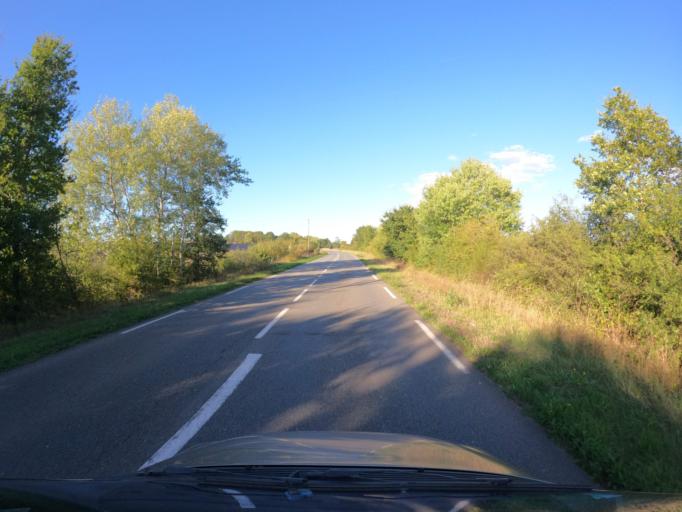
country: FR
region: Bourgogne
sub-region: Departement de Saone-et-Loire
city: Saint-Eusebe
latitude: 46.7353
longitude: 4.4427
